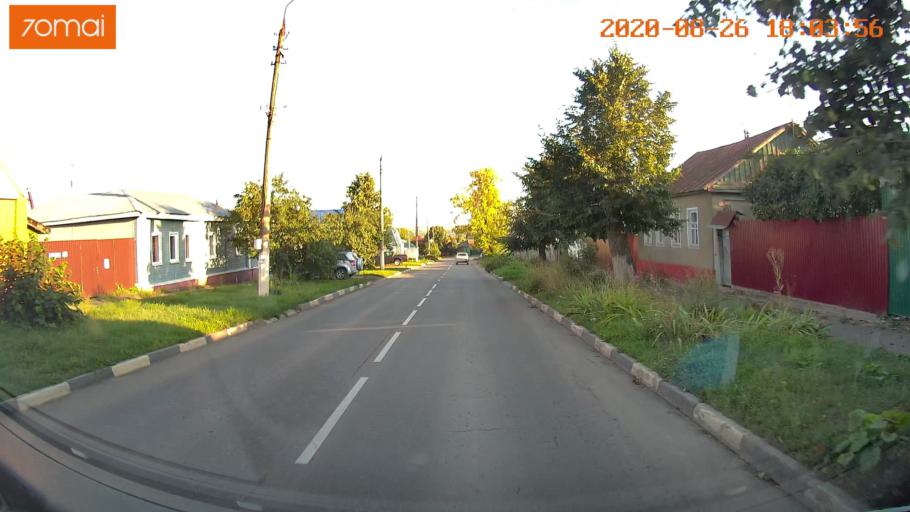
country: RU
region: Tula
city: Yefremov
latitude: 53.1398
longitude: 38.1136
